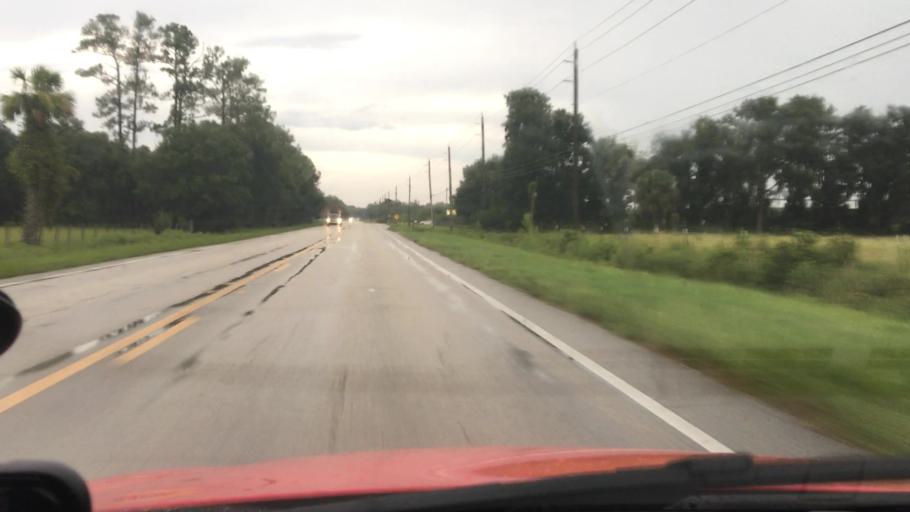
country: US
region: Florida
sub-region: Volusia County
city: Samsula-Spruce Creek
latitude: 29.0467
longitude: -81.0676
